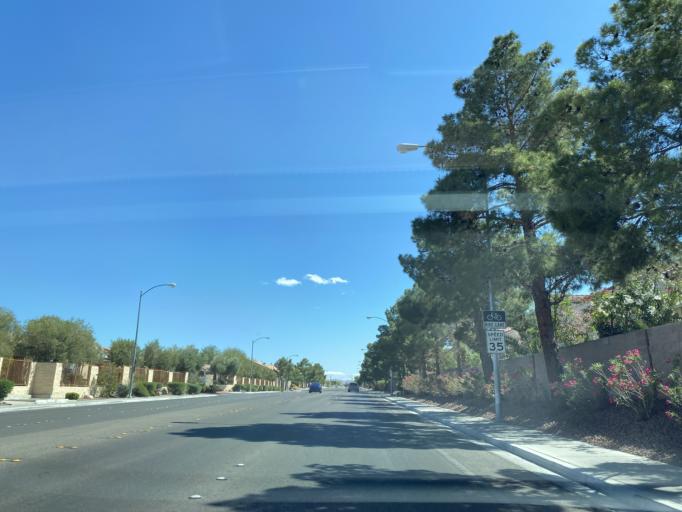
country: US
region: Nevada
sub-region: Clark County
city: Spring Valley
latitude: 36.0926
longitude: -115.2167
